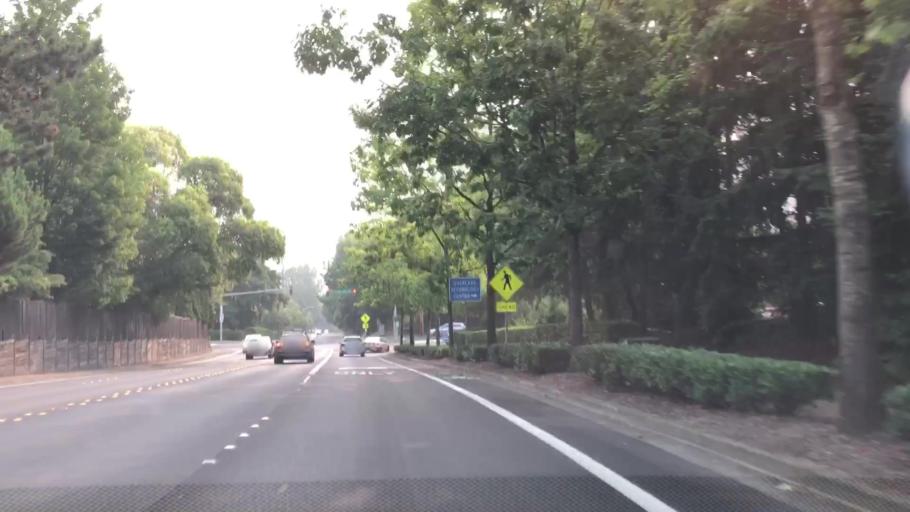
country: US
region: Washington
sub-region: King County
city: Redmond
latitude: 47.6540
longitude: -122.1338
